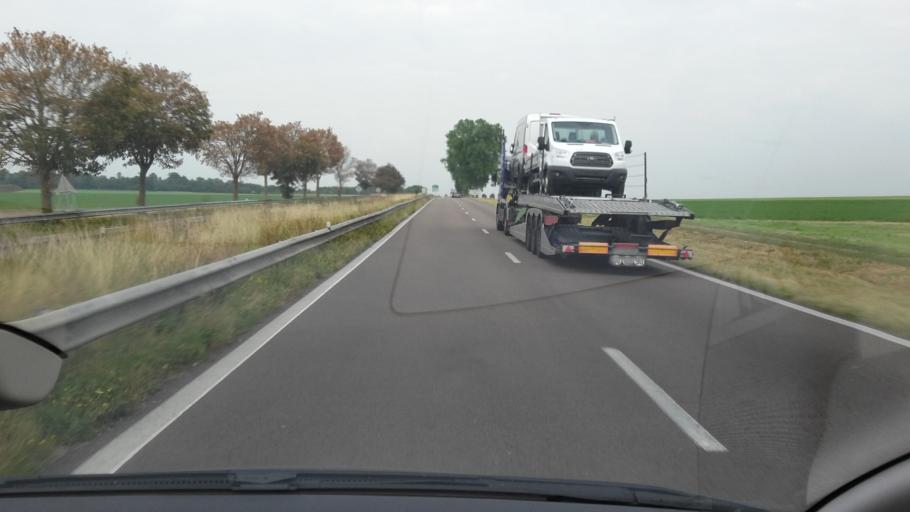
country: FR
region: Champagne-Ardenne
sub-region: Departement de la Marne
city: Bazancourt
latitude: 49.3329
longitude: 4.1728
